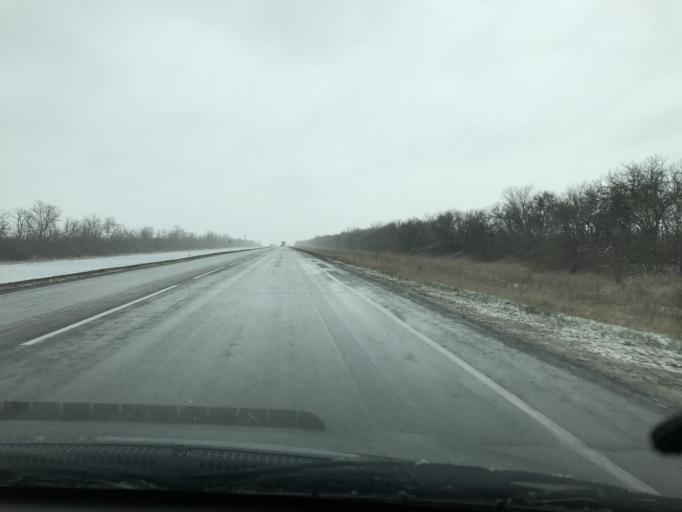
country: RU
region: Rostov
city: Kirovskaya
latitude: 46.9385
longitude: 40.0903
